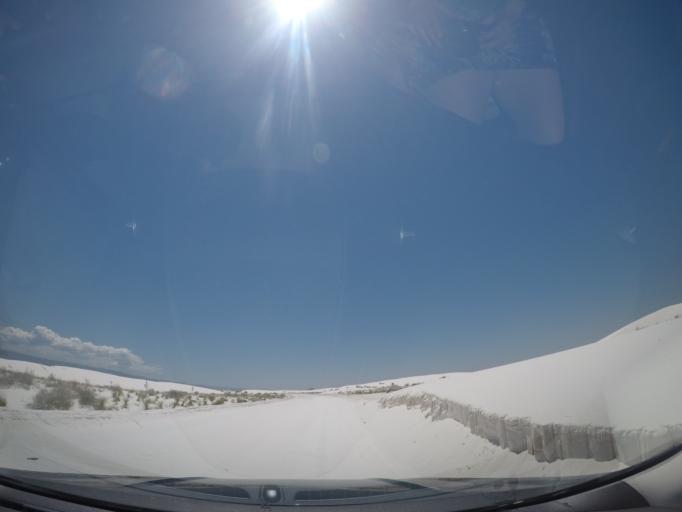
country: US
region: New Mexico
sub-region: Otero County
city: Holloman Air Force Base
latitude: 32.7999
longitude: -106.2534
